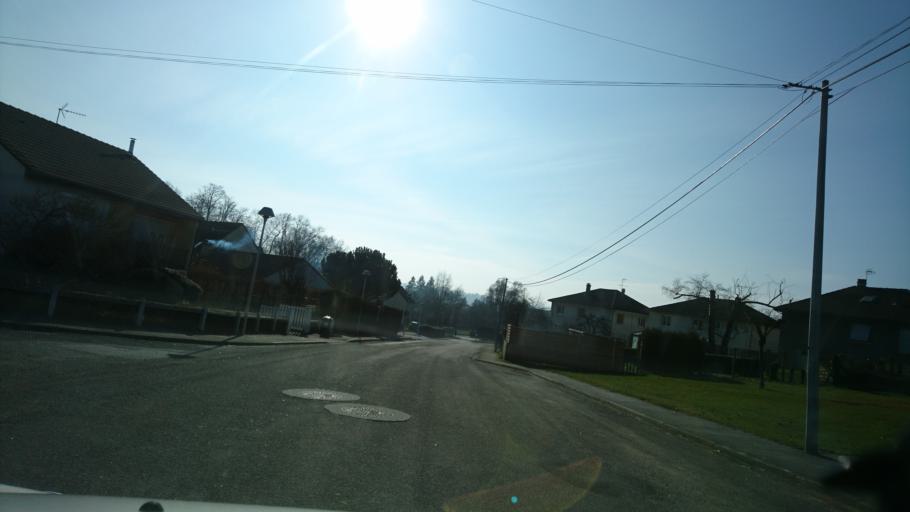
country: FR
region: Limousin
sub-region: Departement de la Haute-Vienne
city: Le Palais-sur-Vienne
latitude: 45.8691
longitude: 1.3163
